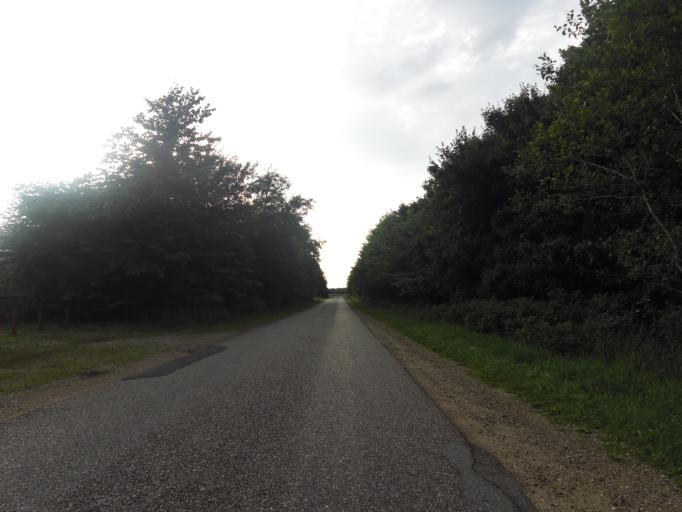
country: DK
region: South Denmark
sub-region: Tonder Kommune
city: Logumkloster
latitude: 55.1546
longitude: 8.9398
